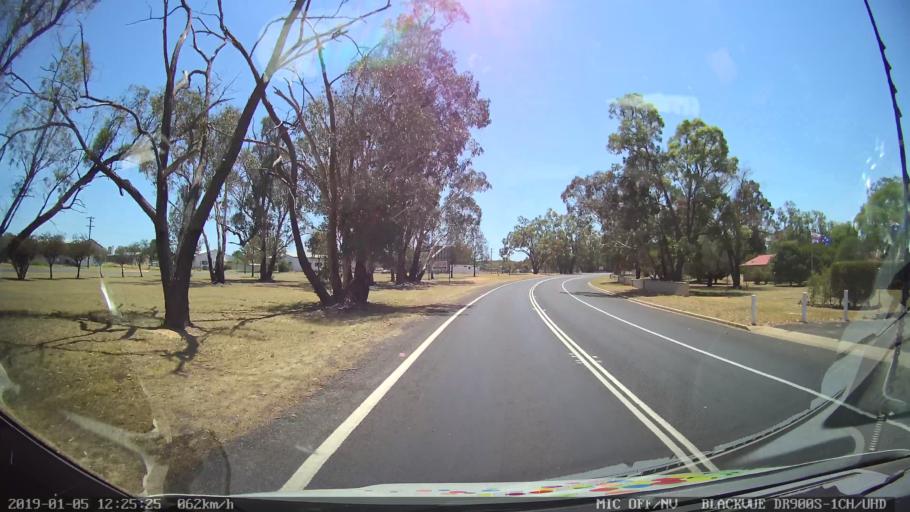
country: AU
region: New South Wales
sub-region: Warrumbungle Shire
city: Coonabarabran
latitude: -31.2607
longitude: 149.2850
